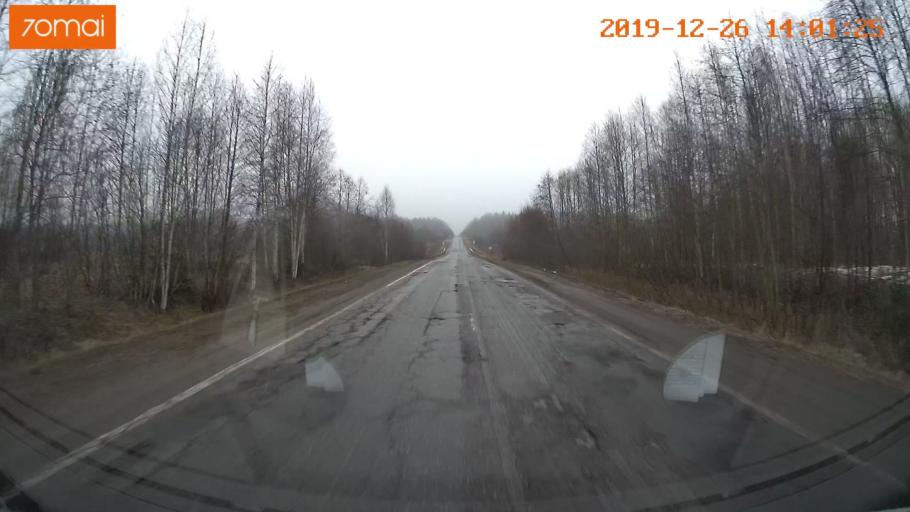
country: RU
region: Jaroslavl
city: Poshekhon'ye
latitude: 58.5506
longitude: 38.7636
